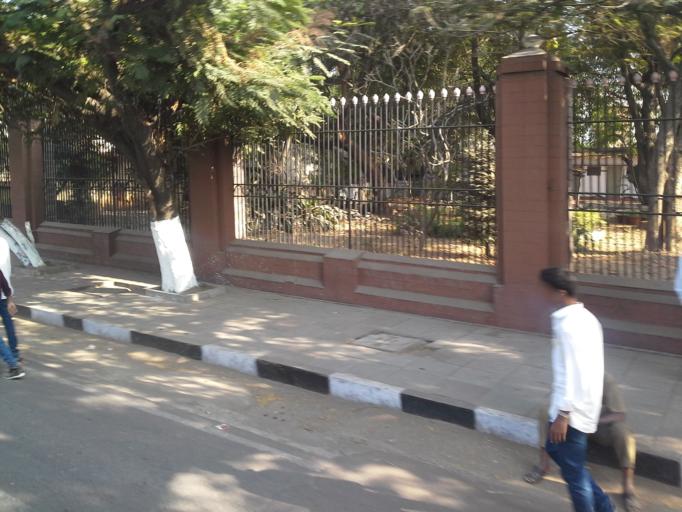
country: IN
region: Telangana
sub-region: Hyderabad
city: Hyderabad
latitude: 17.3725
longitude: 78.4813
